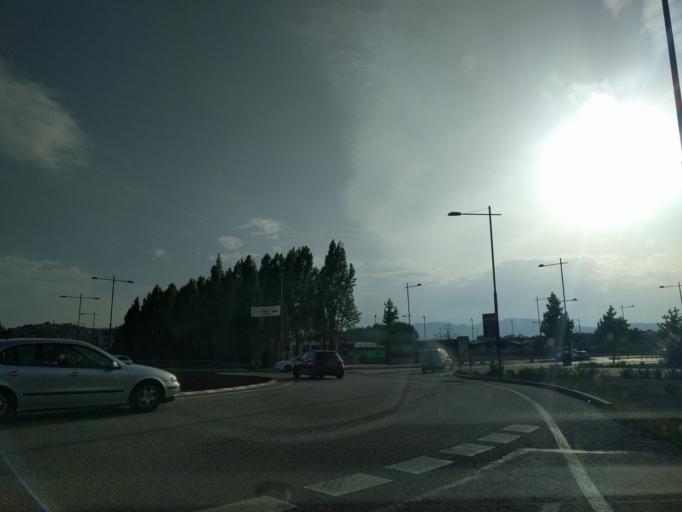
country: ES
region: Catalonia
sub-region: Provincia de Barcelona
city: Tordera
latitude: 41.6957
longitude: 2.7254
